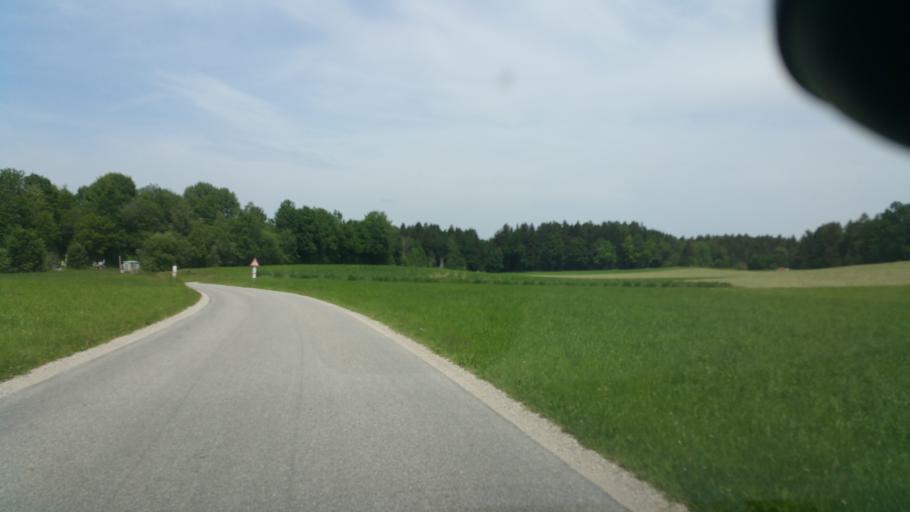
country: DE
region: Bavaria
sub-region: Upper Bavaria
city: Aschau im Chiemgau
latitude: 47.7961
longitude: 12.3262
